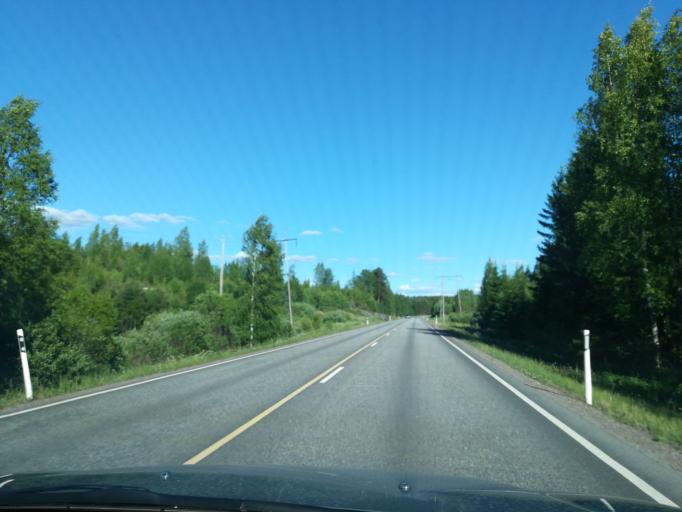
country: FI
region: South Karelia
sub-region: Imatra
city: Ruokolahti
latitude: 61.3505
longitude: 28.7502
